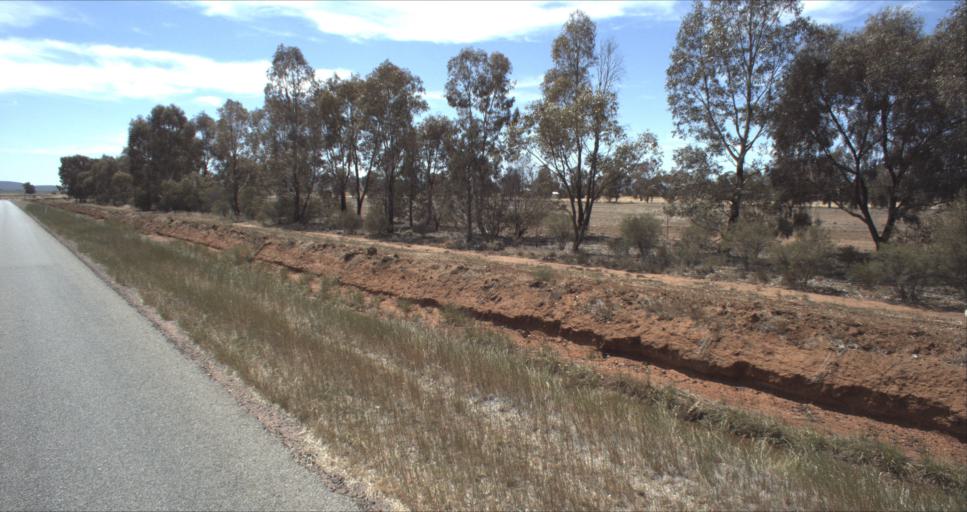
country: AU
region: New South Wales
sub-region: Leeton
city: Leeton
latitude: -34.5593
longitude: 146.4531
